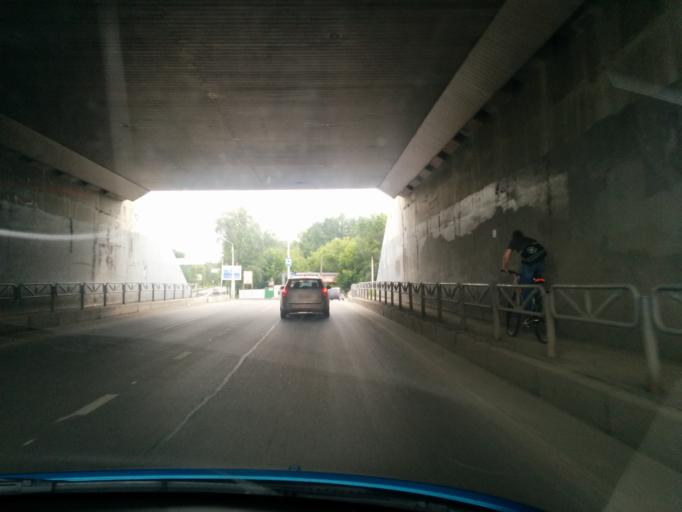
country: RU
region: Perm
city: Perm
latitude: 58.0032
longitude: 56.1943
